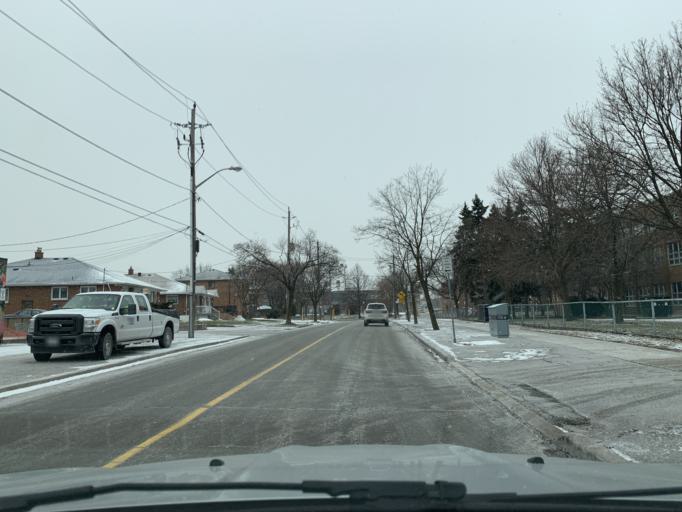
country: CA
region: Ontario
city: Toronto
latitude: 43.7286
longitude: -79.4779
